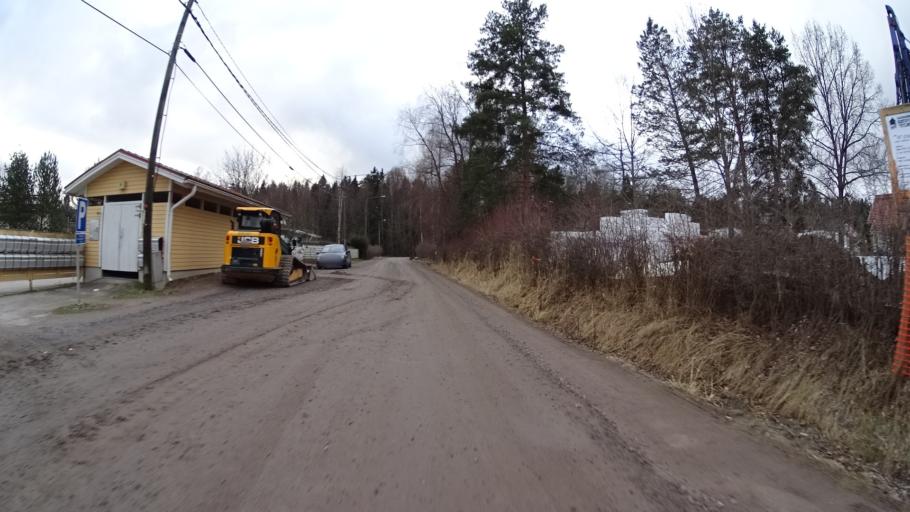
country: FI
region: Uusimaa
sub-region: Helsinki
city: Kilo
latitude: 60.2357
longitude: 24.7680
